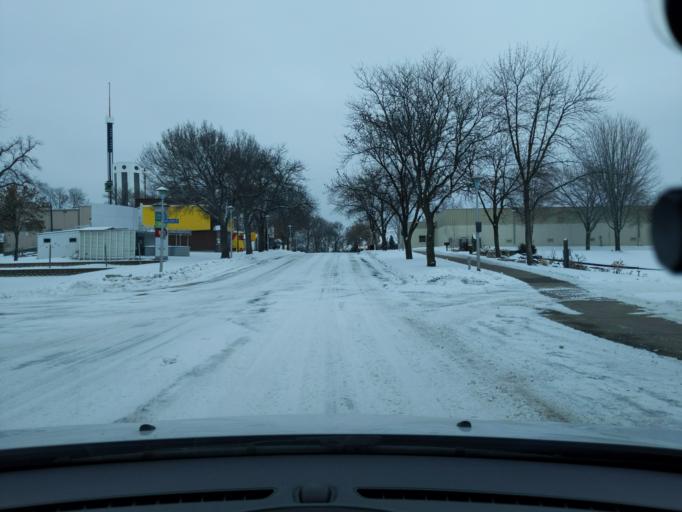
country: US
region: Minnesota
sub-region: Ramsey County
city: Falcon Heights
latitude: 44.9786
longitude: -93.1724
